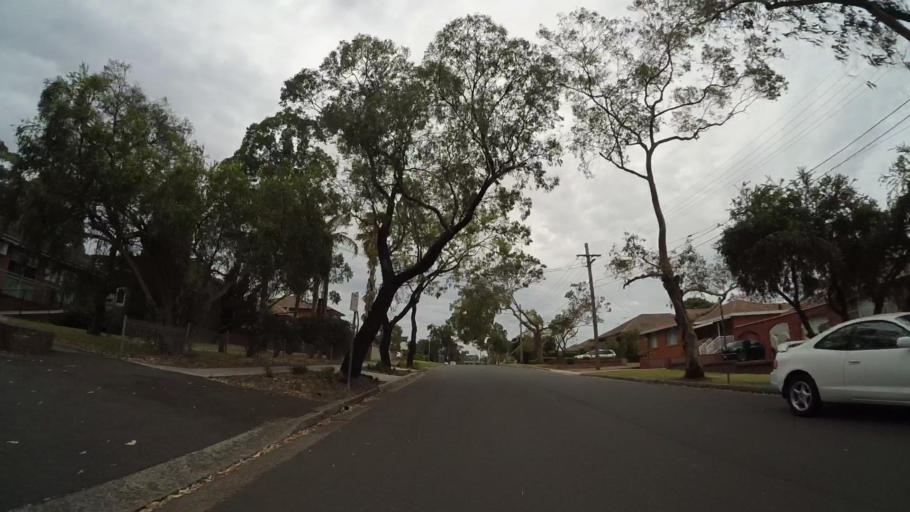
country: AU
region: New South Wales
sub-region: Sutherland Shire
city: Gymea
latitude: -34.0259
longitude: 151.0892
